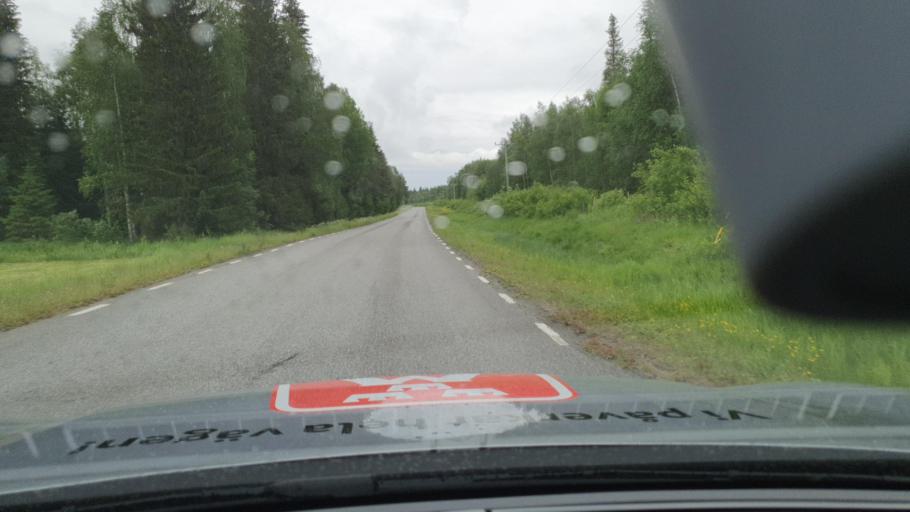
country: SE
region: Norrbotten
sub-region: Kalix Kommun
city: Toere
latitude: 65.8956
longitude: 22.6301
